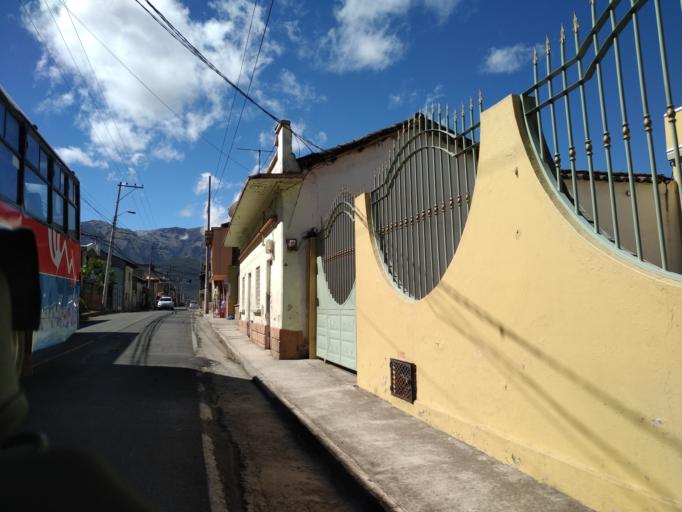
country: EC
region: Imbabura
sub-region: Canton Otavalo
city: Otavalo
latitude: 0.2087
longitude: -78.2038
